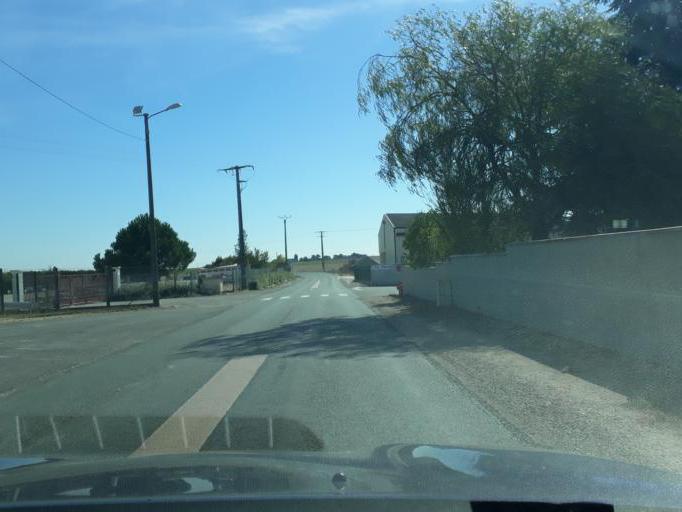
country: FR
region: Centre
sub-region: Departement du Loir-et-Cher
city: Ouzouer-le-Marche
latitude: 47.8848
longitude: 1.5495
